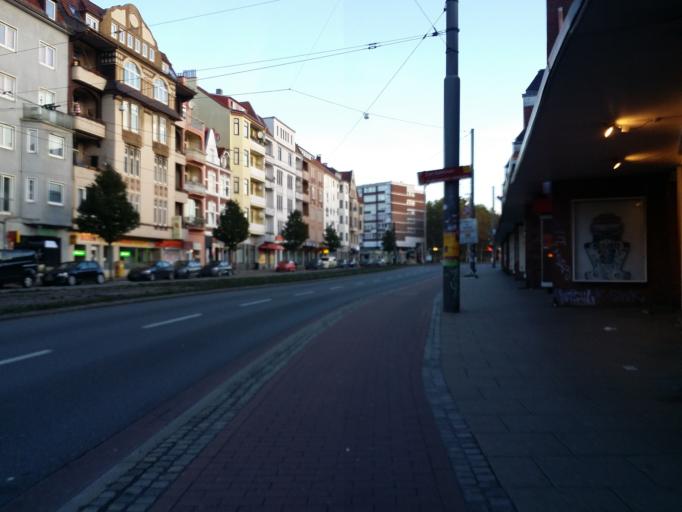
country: DE
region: Bremen
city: Bremen
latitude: 53.0703
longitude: 8.8001
